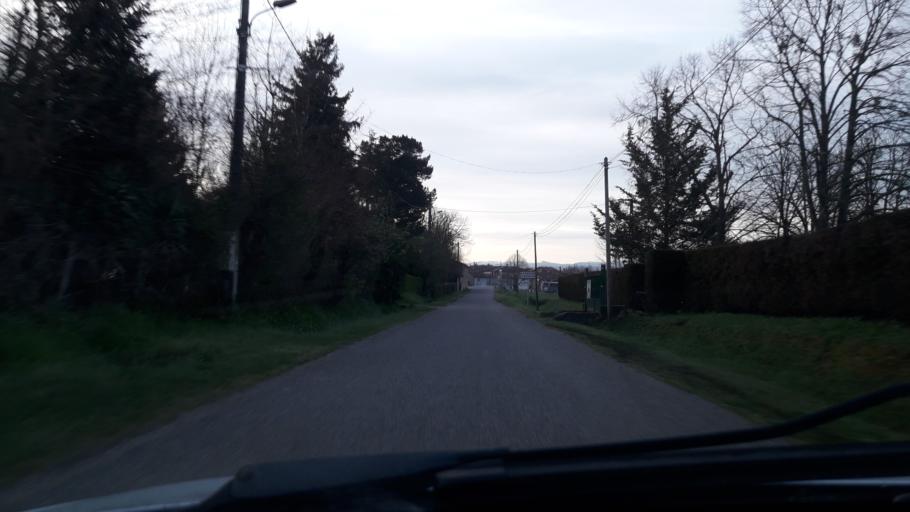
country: FR
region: Midi-Pyrenees
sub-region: Departement de la Haute-Garonne
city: Montesquieu-Volvestre
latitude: 43.1692
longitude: 1.2739
